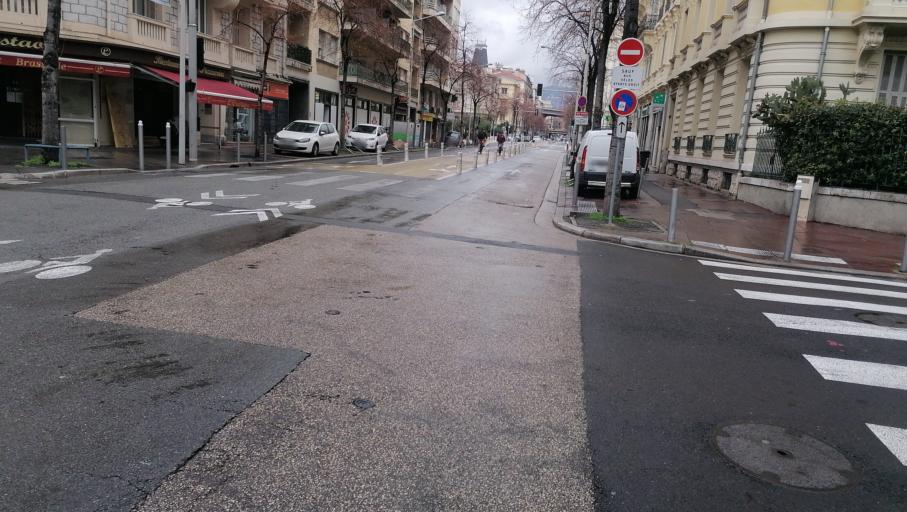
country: FR
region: Provence-Alpes-Cote d'Azur
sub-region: Departement des Alpes-Maritimes
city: Nice
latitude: 43.6985
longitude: 7.2563
